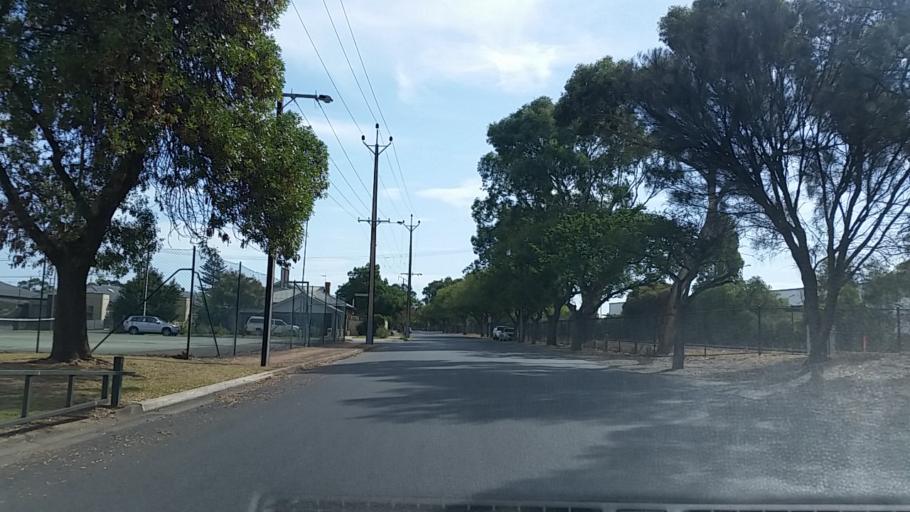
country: AU
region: South Australia
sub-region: Charles Sturt
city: Woodville North
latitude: -34.8761
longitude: 138.5347
